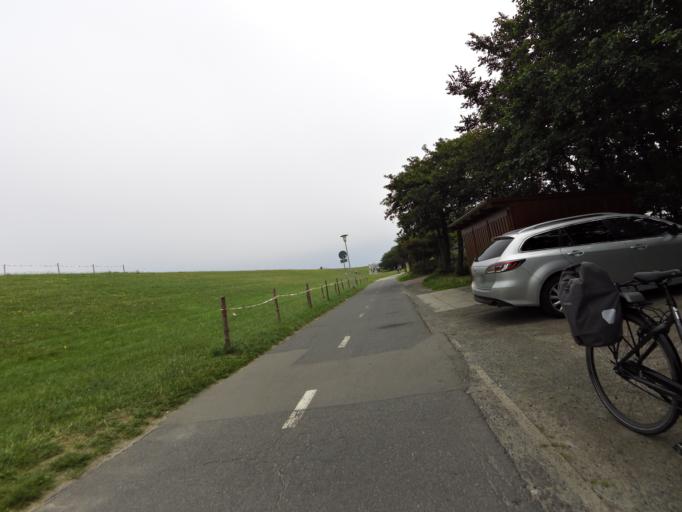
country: DE
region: Lower Saxony
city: Cuxhaven
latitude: 53.8911
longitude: 8.6769
